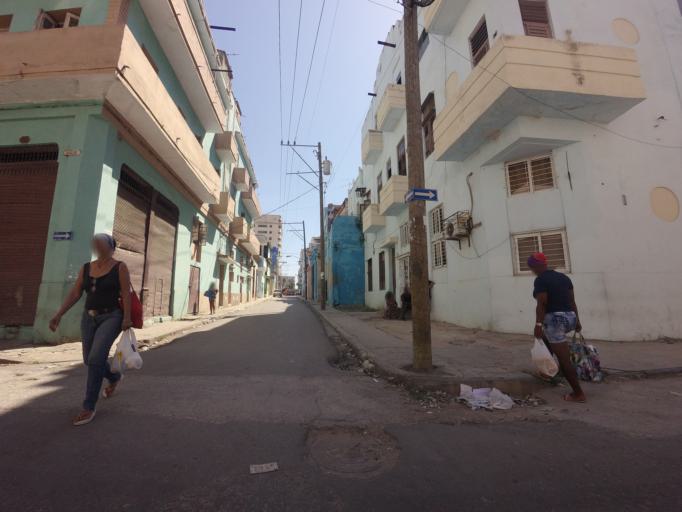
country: CU
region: La Habana
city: Centro Habana
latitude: 23.1337
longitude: -82.3705
